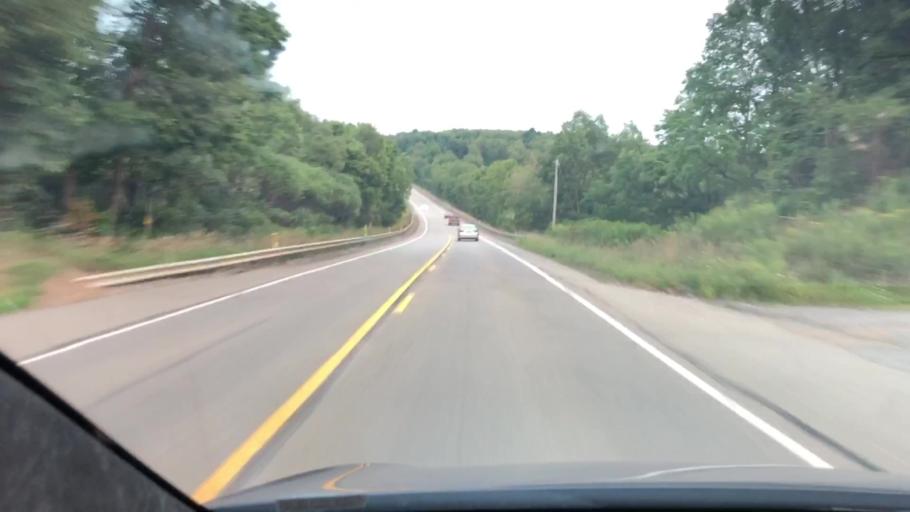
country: US
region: Pennsylvania
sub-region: Butler County
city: Shanor-Northvue
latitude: 40.9164
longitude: -79.9429
